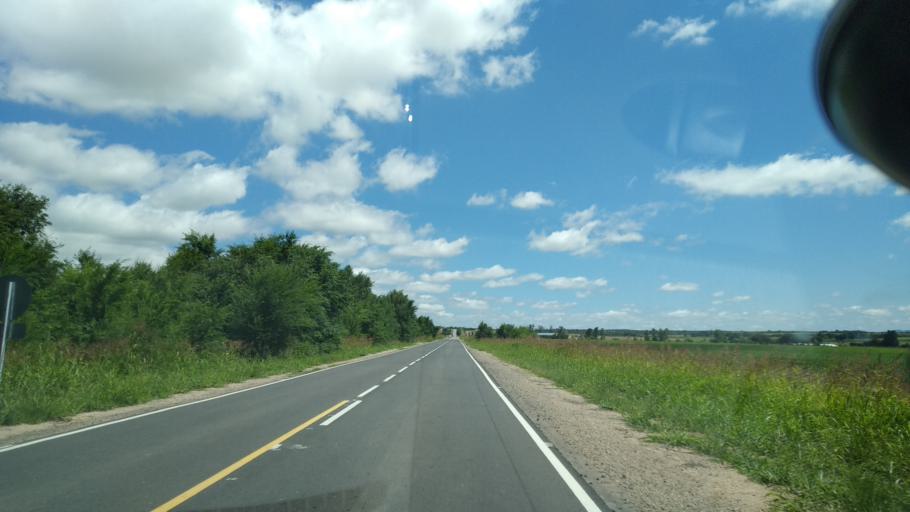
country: AR
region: Cordoba
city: Villa Cura Brochero
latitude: -31.6448
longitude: -65.1015
